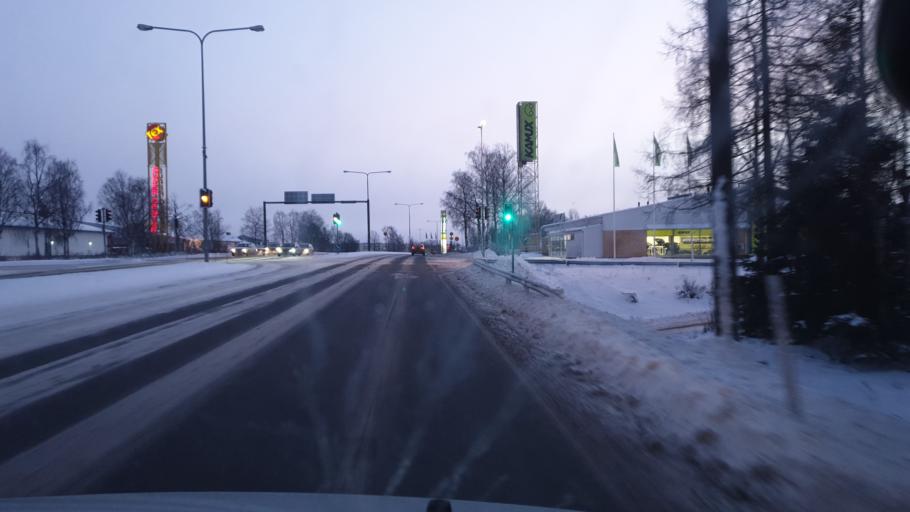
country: FI
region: Lapland
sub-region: Kemi-Tornio
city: Tornio
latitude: 65.8431
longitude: 24.1857
